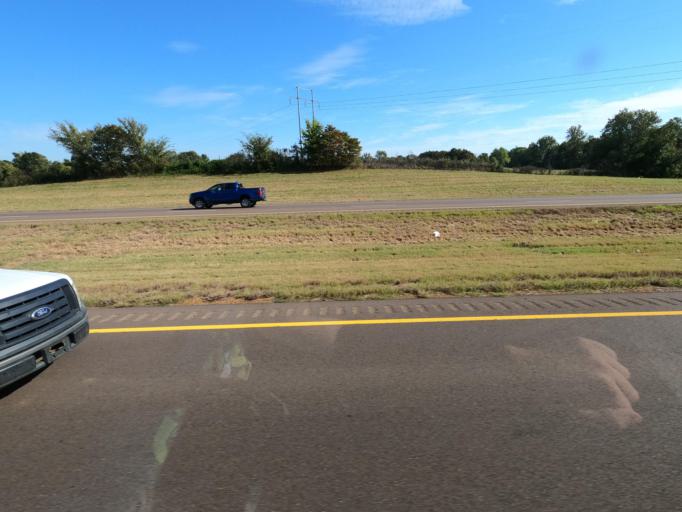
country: US
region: Tennessee
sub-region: Obion County
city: Troy
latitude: 36.3217
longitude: -89.1828
